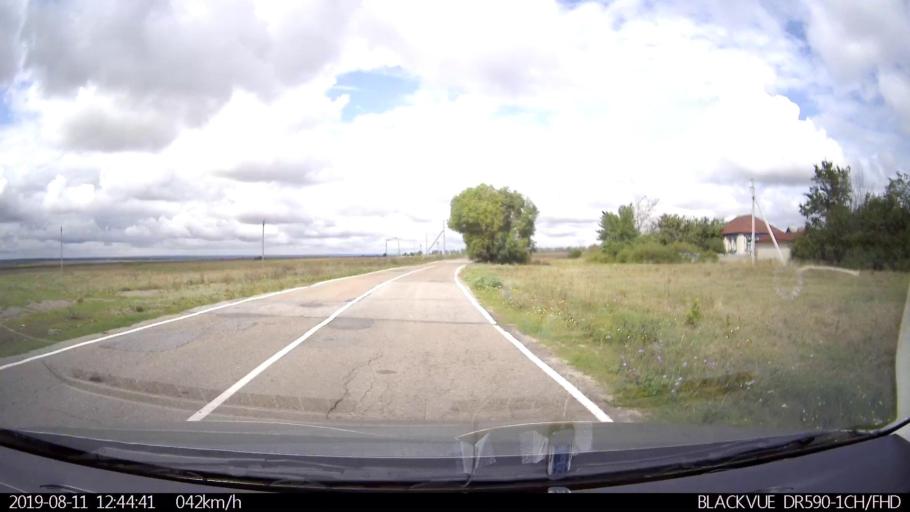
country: RU
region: Ulyanovsk
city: Ignatovka
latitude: 53.8559
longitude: 47.7340
